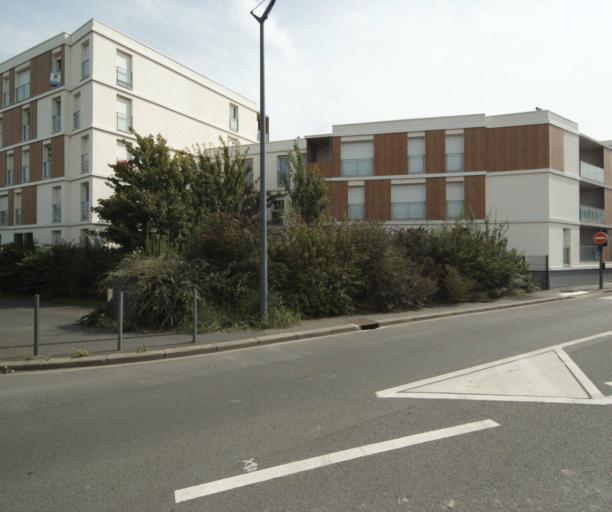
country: FR
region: Nord-Pas-de-Calais
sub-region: Departement du Nord
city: Wattignies
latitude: 50.6030
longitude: 3.0405
